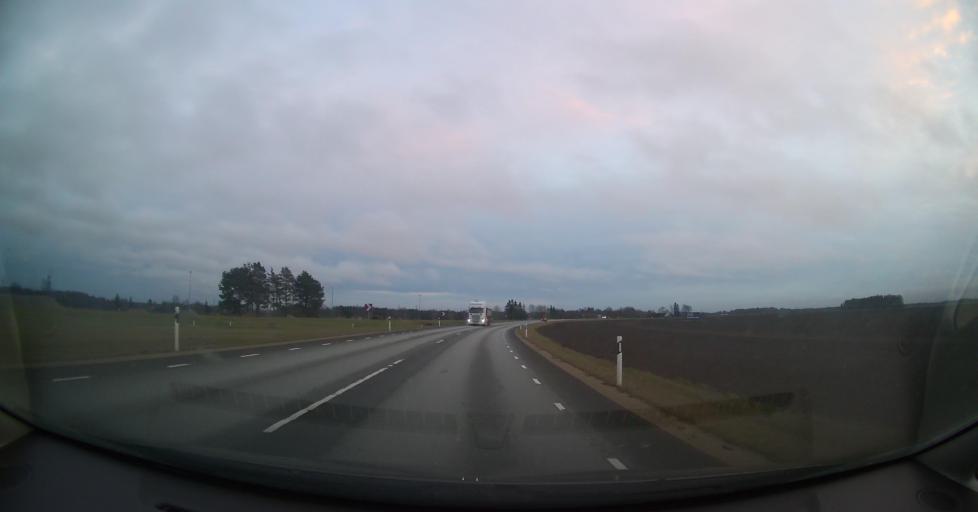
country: EE
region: Laeaene-Virumaa
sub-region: Haljala vald
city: Haljala
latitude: 59.4216
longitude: 26.2757
